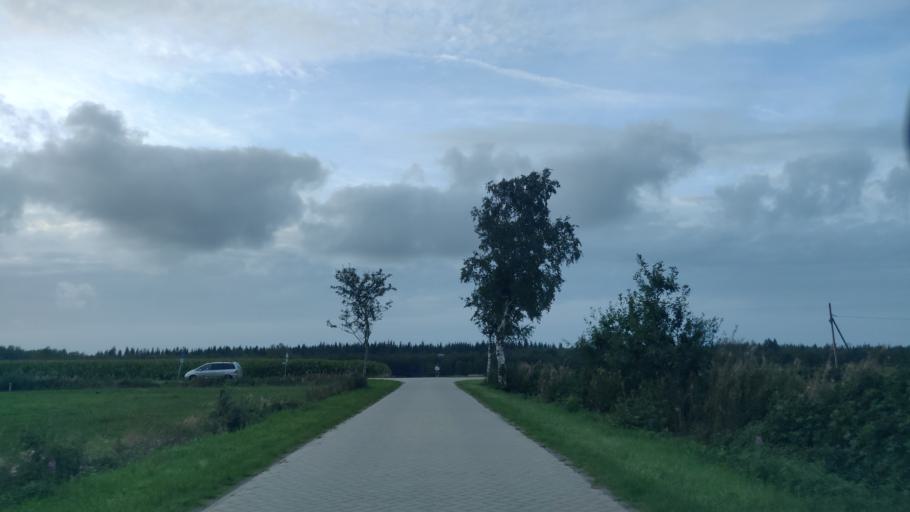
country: DE
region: Lower Saxony
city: Aurich
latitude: 53.5042
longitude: 7.4278
